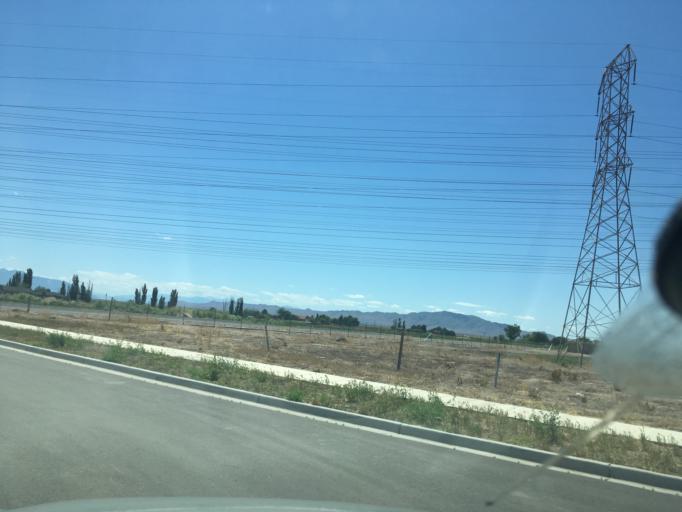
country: US
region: Utah
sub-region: Davis County
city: Layton
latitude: 41.0497
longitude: -111.9993
